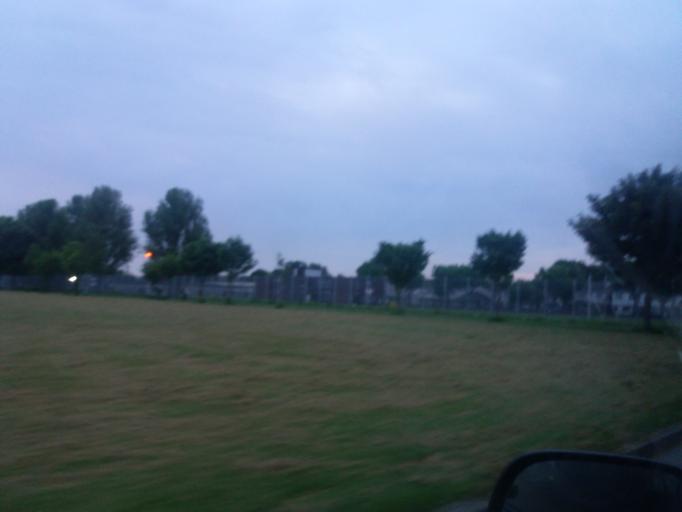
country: IE
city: Darndale
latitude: 53.3936
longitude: -6.1854
